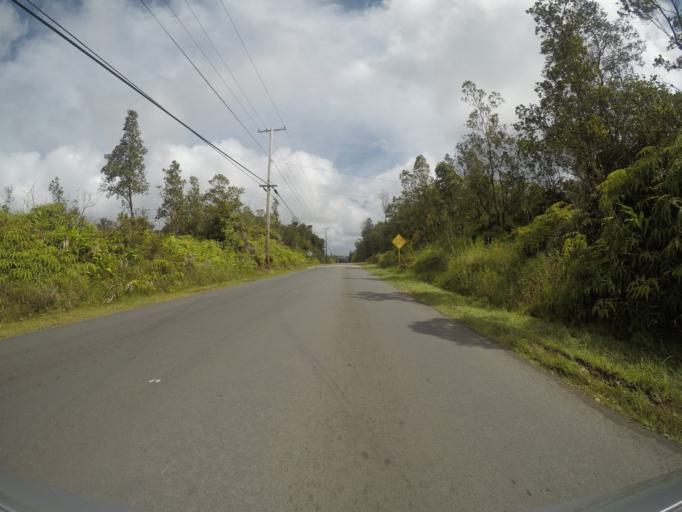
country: US
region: Hawaii
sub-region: Hawaii County
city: Fern Acres
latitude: 19.4750
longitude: -155.1400
